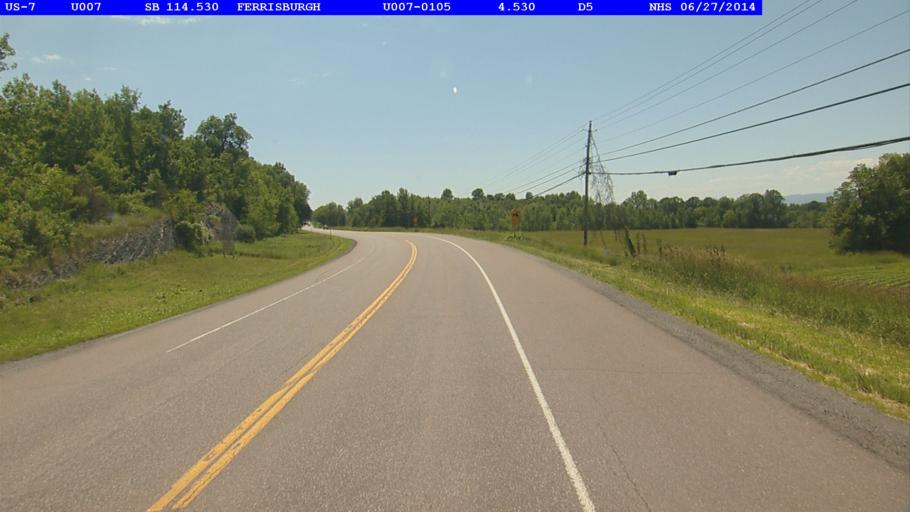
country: US
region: Vermont
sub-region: Addison County
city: Vergennes
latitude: 44.2251
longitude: -73.2379
